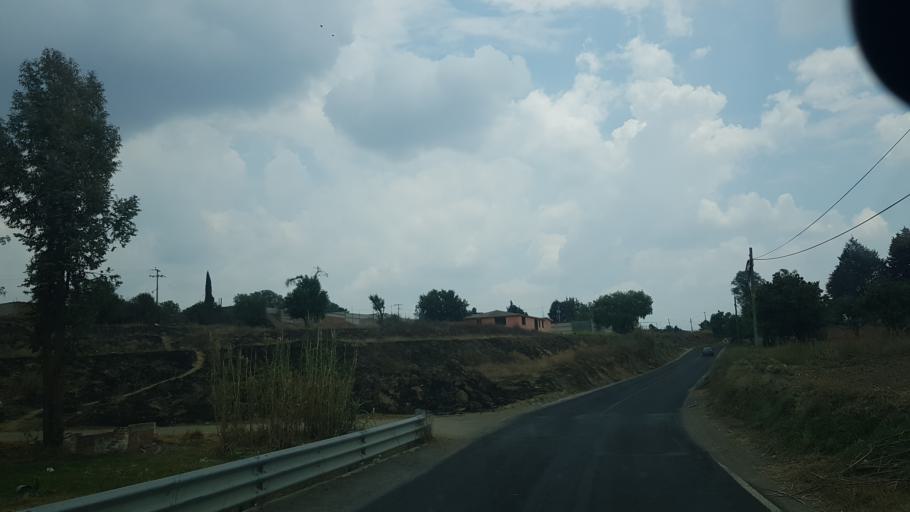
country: MX
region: Puebla
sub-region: Huejotzingo
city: San Miguel Tianguizolco
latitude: 19.1602
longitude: -98.4324
